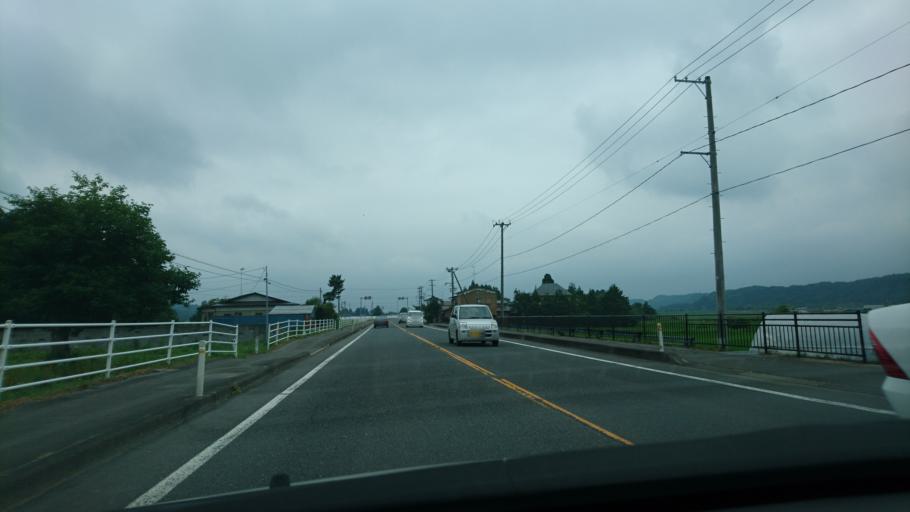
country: JP
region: Miyagi
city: Furukawa
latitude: 38.6973
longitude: 140.8436
